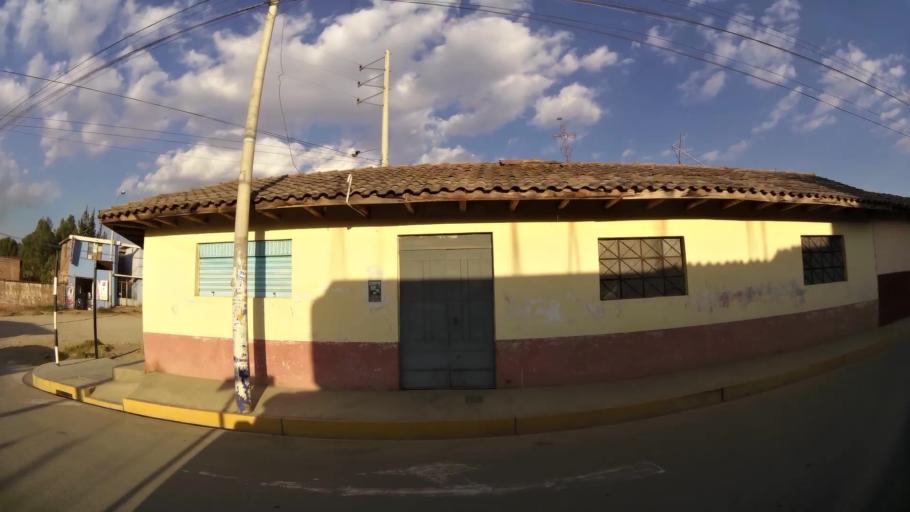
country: PE
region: Junin
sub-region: Provincia de Huancayo
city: Pilcomay
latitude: -12.0313
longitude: -75.2295
